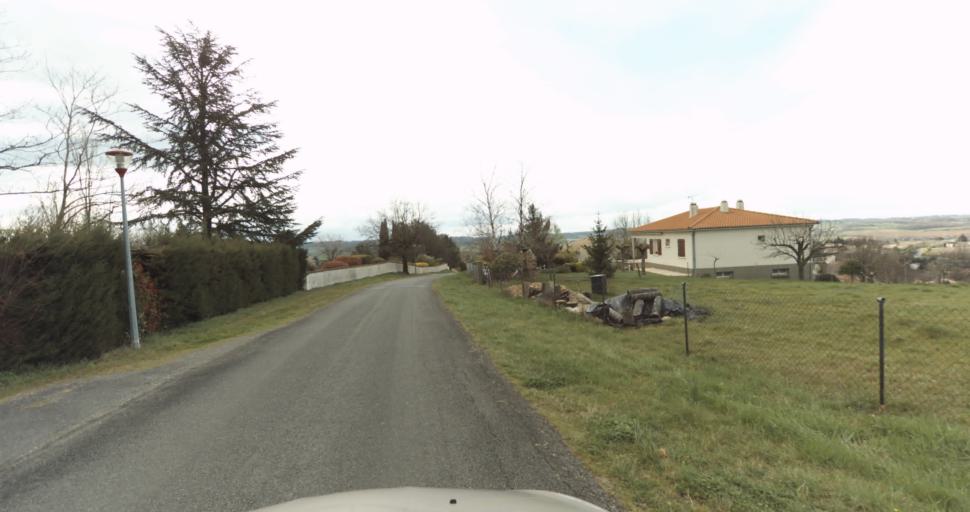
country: FR
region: Midi-Pyrenees
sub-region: Departement du Tarn
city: Puygouzon
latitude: 43.9006
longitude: 2.1766
